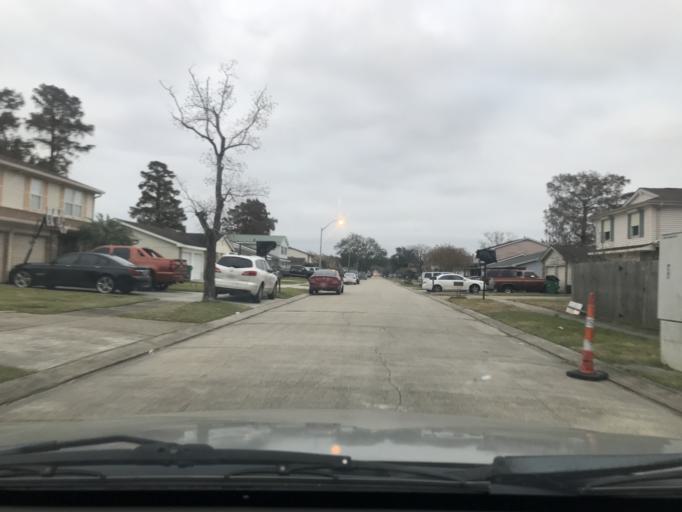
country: US
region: Louisiana
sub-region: Jefferson Parish
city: Woodmere
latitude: 29.8587
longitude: -90.0774
